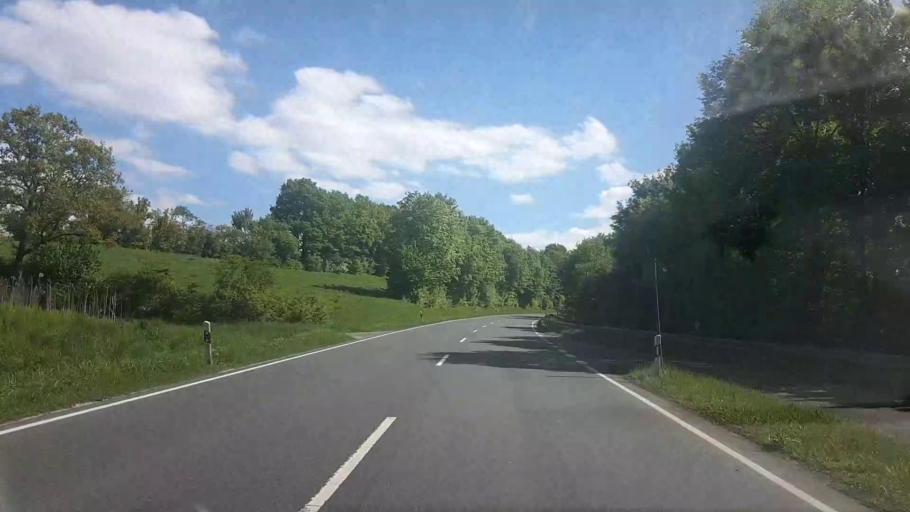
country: DE
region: Bavaria
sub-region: Upper Franconia
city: Rattelsdorf
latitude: 50.0590
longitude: 10.8778
